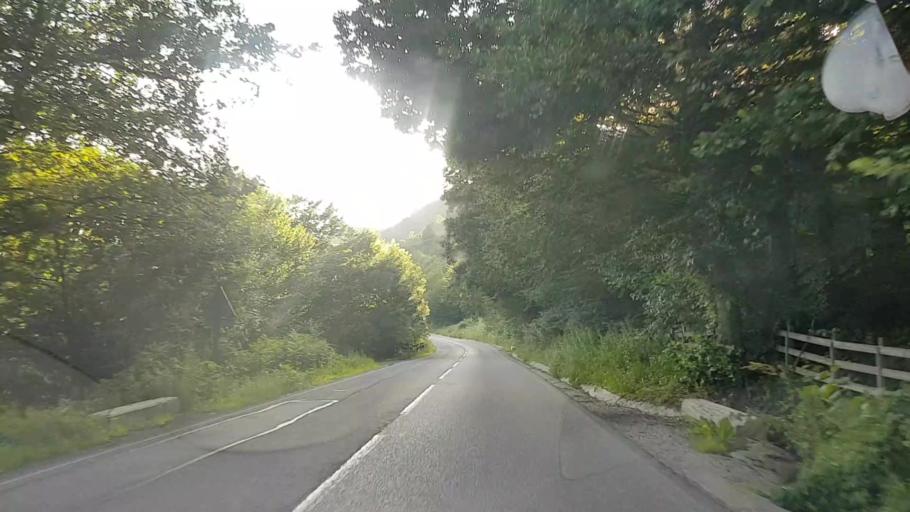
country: RO
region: Harghita
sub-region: Comuna Praid
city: Ocna de Sus
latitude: 46.5731
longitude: 25.2058
